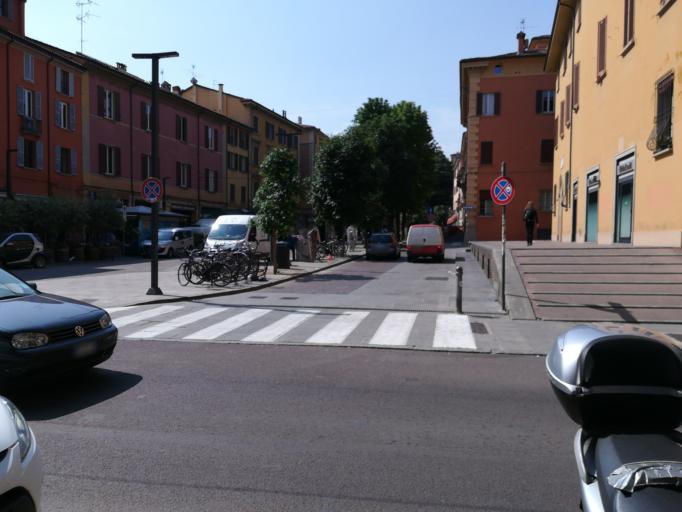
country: IT
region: Emilia-Romagna
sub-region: Provincia di Bologna
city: Bologna
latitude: 44.4941
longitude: 11.3517
